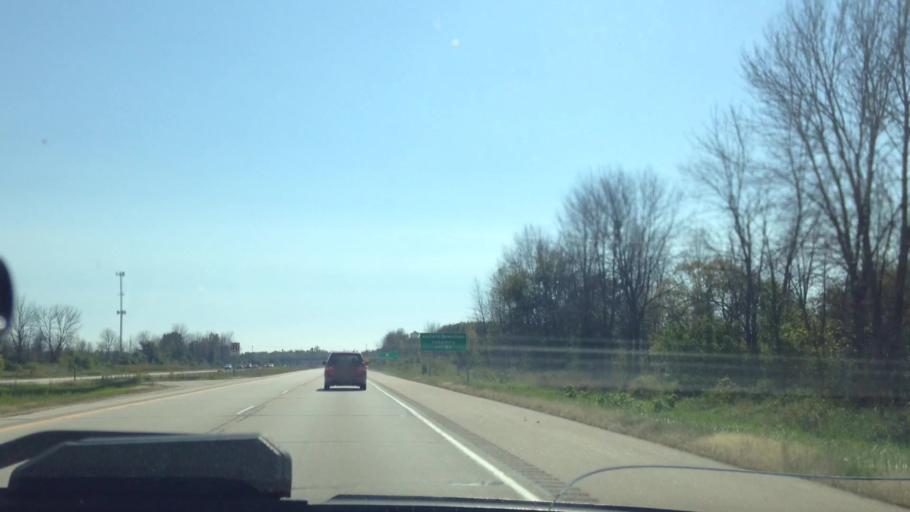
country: US
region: Wisconsin
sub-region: Ozaukee County
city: Grafton
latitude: 43.2872
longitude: -87.9214
